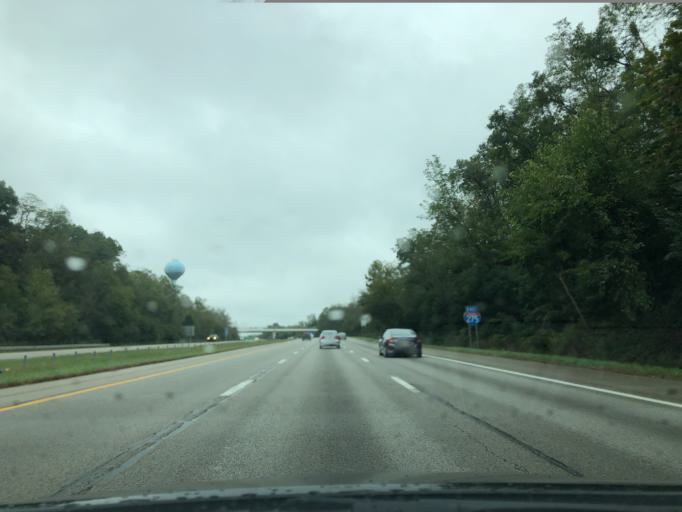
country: US
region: Ohio
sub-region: Hamilton County
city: The Village of Indian Hill
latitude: 39.2368
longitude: -84.2956
